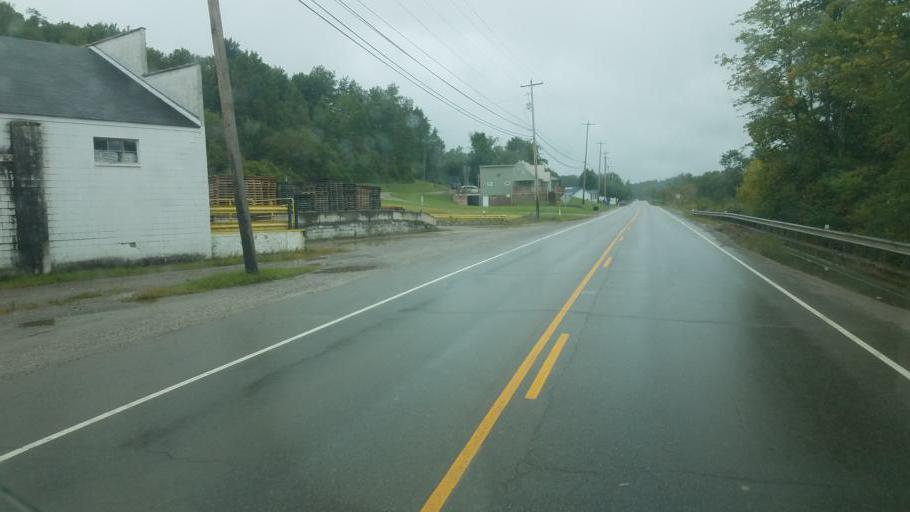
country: US
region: Ohio
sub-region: Jackson County
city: Oak Hill
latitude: 38.8875
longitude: -82.5749
